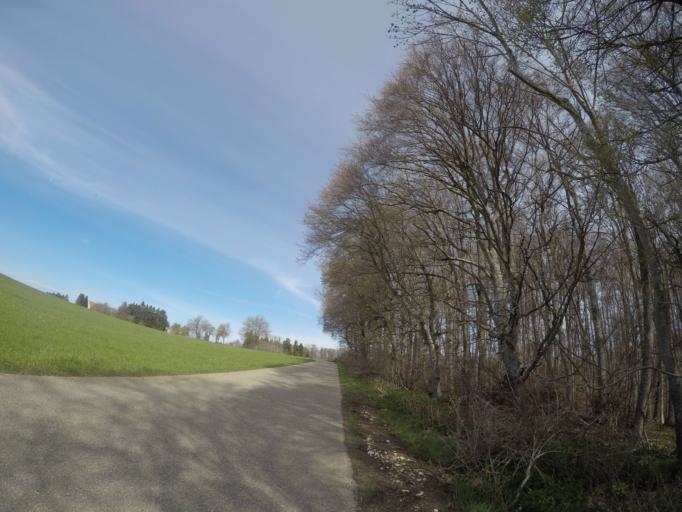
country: DE
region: Baden-Wuerttemberg
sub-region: Regierungsbezirk Stuttgart
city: Hohenstadt
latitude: 48.5397
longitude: 9.6431
